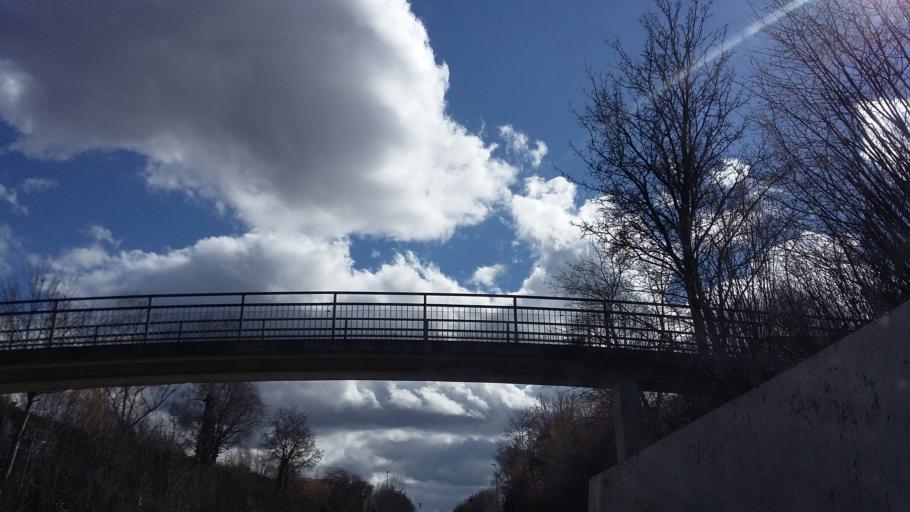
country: DE
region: Bavaria
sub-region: Upper Bavaria
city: Germering
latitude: 48.1303
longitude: 11.3761
